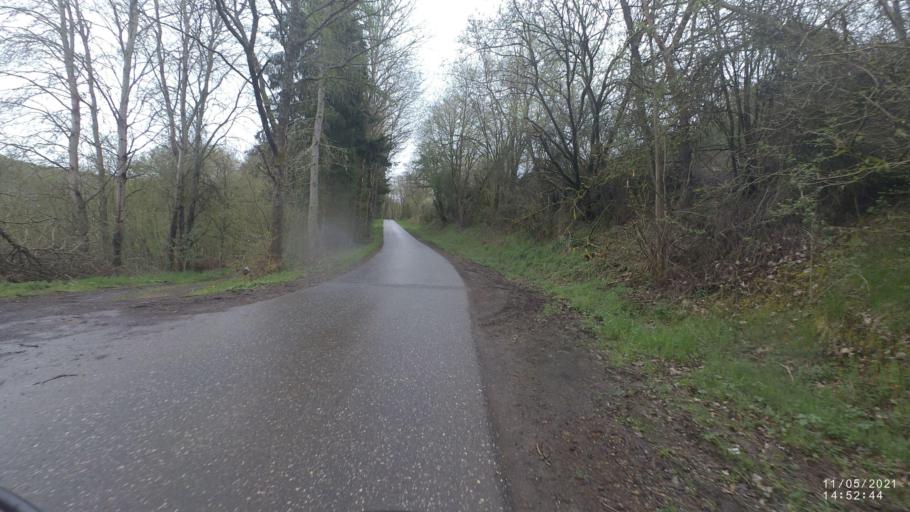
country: DE
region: Rheinland-Pfalz
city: Ditscheid
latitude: 50.2957
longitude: 7.0783
